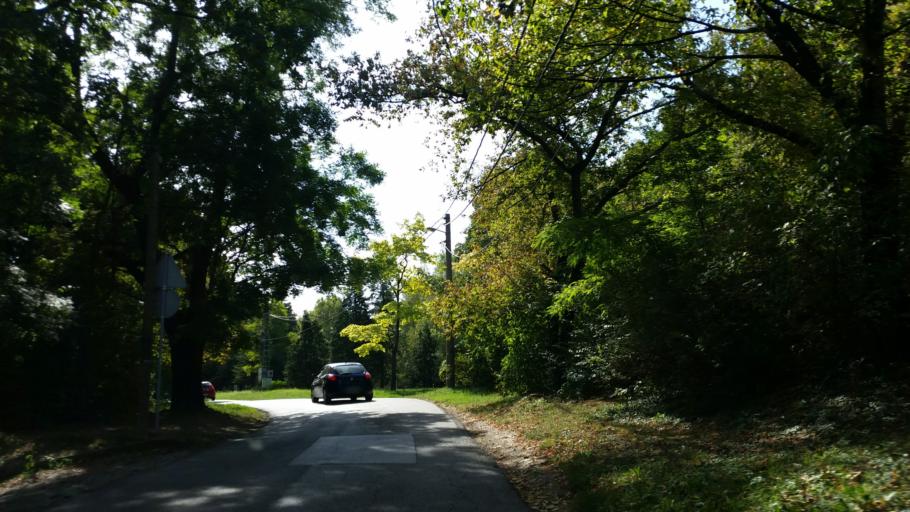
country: RS
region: Central Serbia
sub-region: Belgrade
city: Palilula
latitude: 44.8065
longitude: 20.5100
